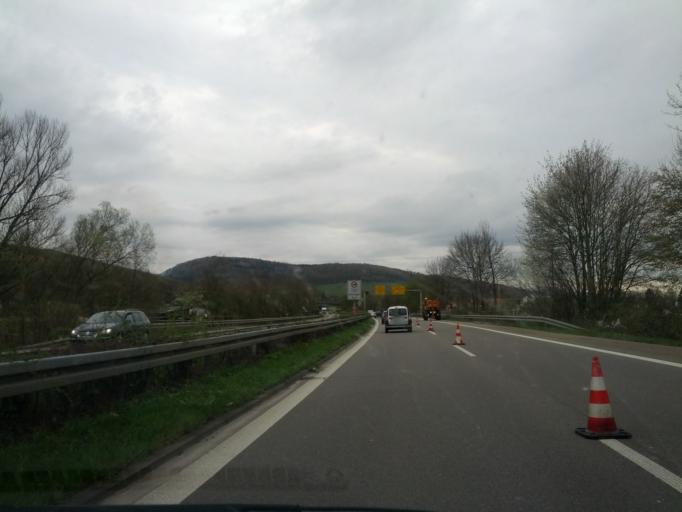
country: DE
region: Baden-Wuerttemberg
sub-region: Freiburg Region
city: Ebringen
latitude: 47.9685
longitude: 7.7697
